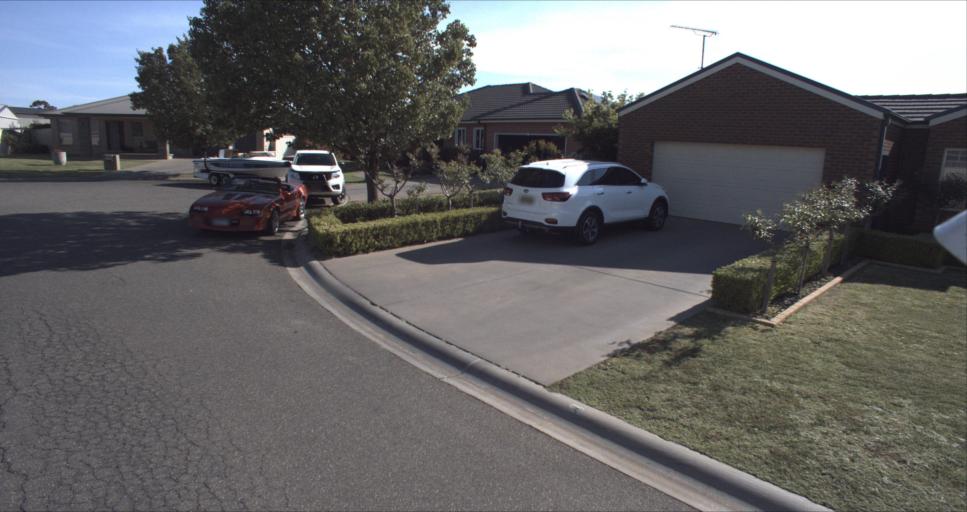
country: AU
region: New South Wales
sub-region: Leeton
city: Leeton
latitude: -34.5374
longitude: 146.4044
